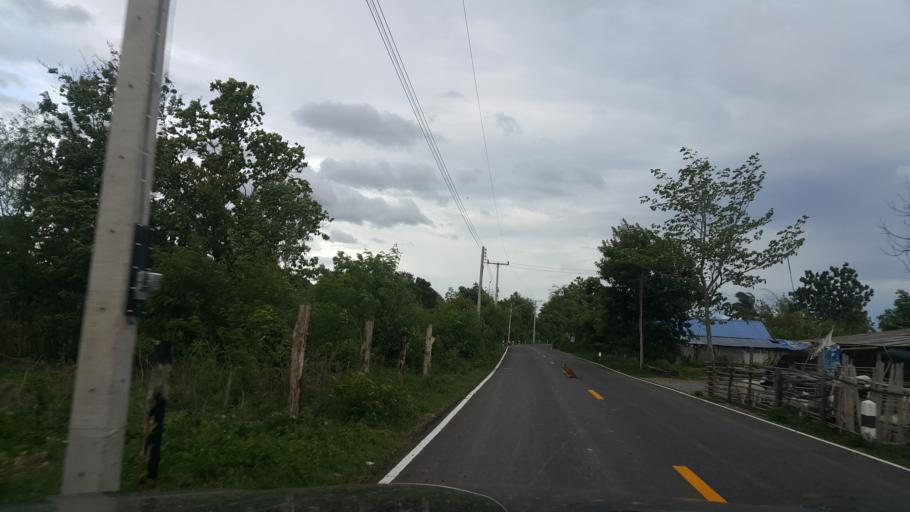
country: TH
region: Sukhothai
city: Thung Saliam
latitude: 17.1707
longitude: 99.4888
